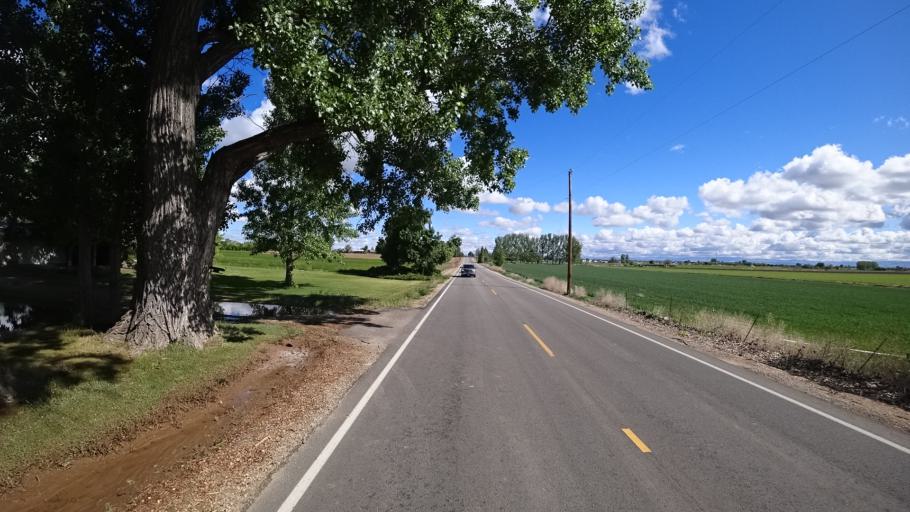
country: US
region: Idaho
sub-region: Ada County
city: Kuna
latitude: 43.4924
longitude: -116.4537
